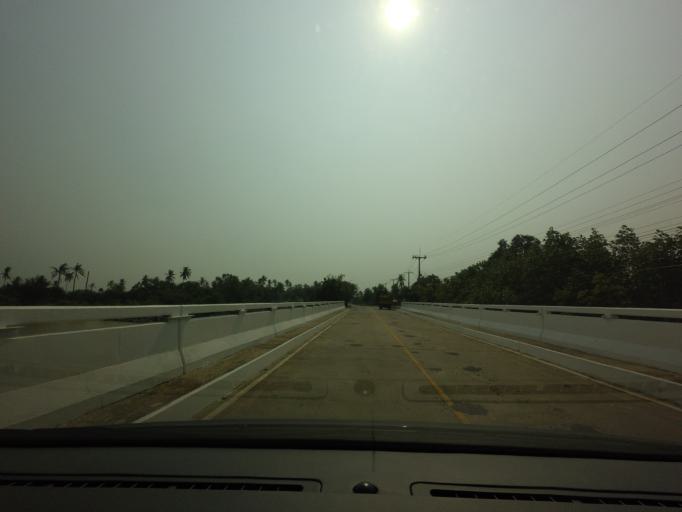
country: TH
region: Prachuap Khiri Khan
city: Kui Buri
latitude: 12.0380
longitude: 99.9015
